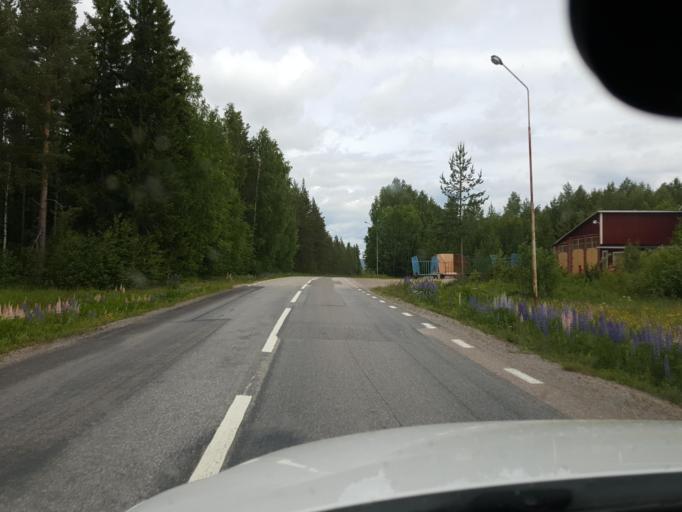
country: SE
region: Gaevleborg
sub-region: Ljusdals Kommun
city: Farila
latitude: 61.7999
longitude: 15.7137
